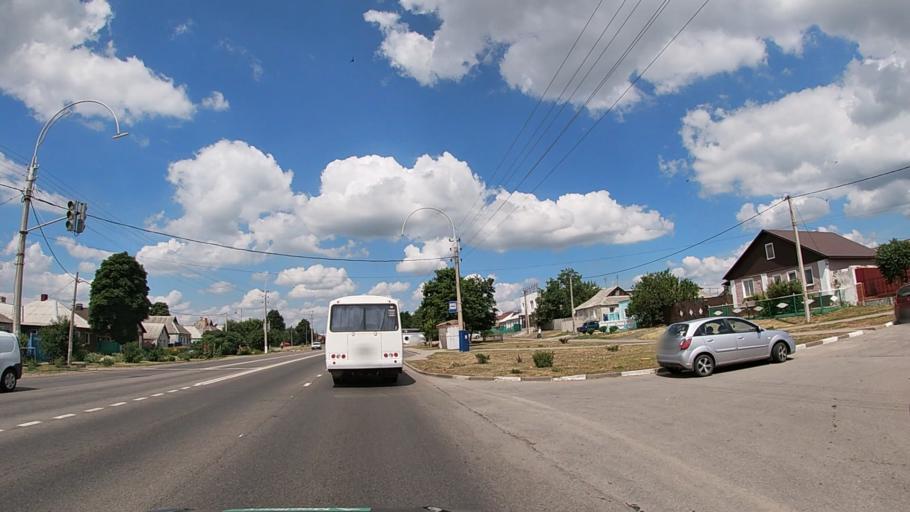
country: RU
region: Belgorod
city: Severnyy
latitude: 50.6251
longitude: 36.4994
